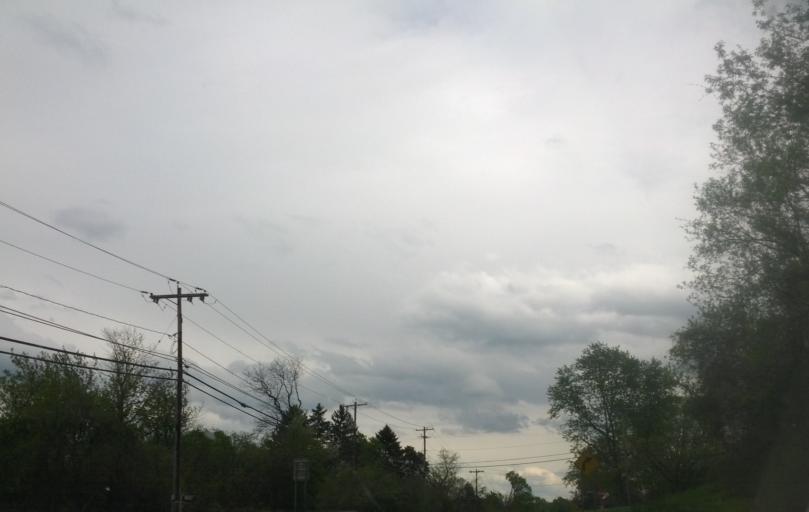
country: US
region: New York
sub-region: Onondaga County
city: Nedrow
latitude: 42.9944
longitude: -76.0986
